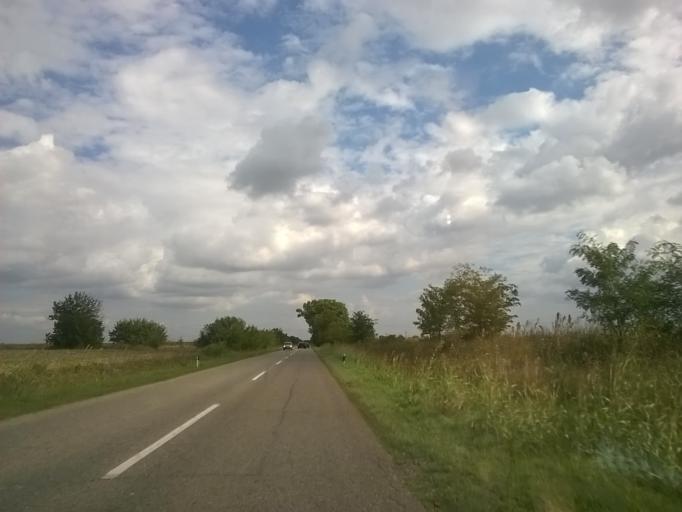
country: RS
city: Padina
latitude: 45.1170
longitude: 20.6836
